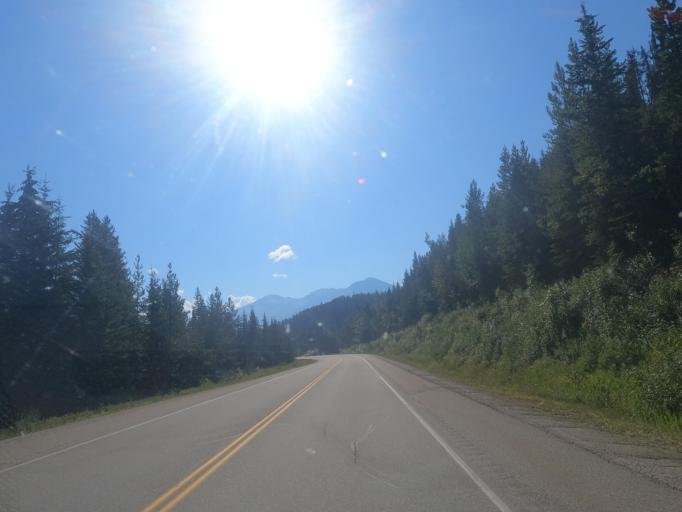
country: CA
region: Alberta
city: Jasper Park Lodge
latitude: 52.8609
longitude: -118.6407
